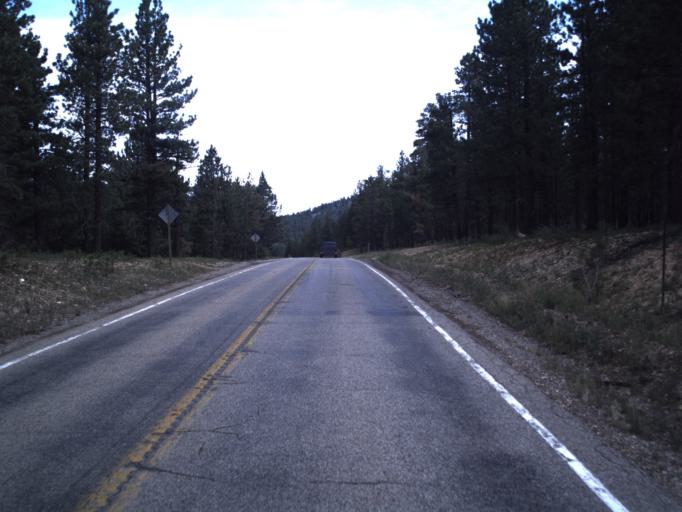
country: US
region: Utah
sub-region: Garfield County
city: Panguitch
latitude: 37.4970
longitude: -112.6210
